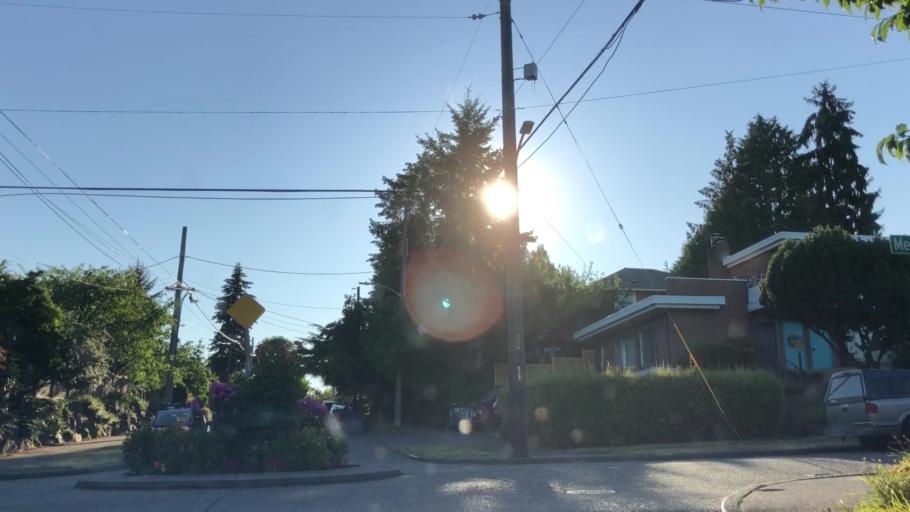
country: US
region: Washington
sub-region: King County
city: Seattle
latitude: 47.6505
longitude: -122.3336
